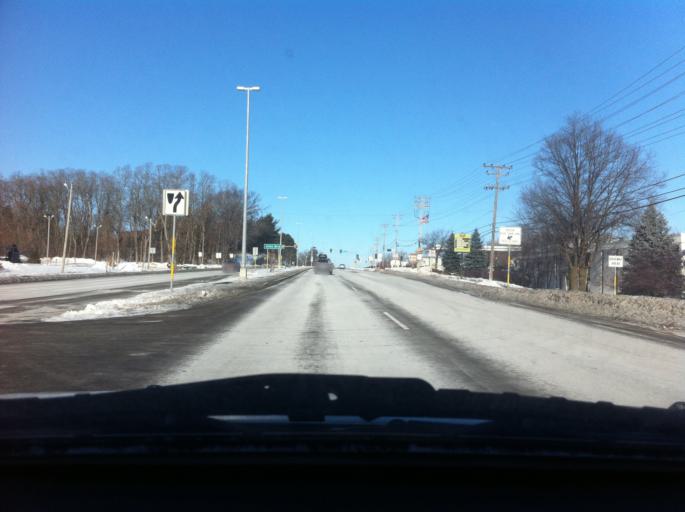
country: US
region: Wisconsin
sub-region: Dane County
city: Middleton
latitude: 43.0881
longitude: -89.4833
